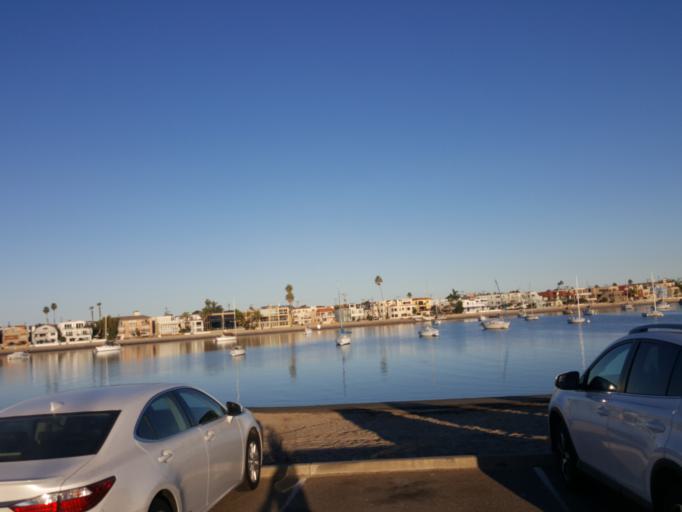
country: US
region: California
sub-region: San Diego County
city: La Jolla
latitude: 32.7790
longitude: -117.2486
